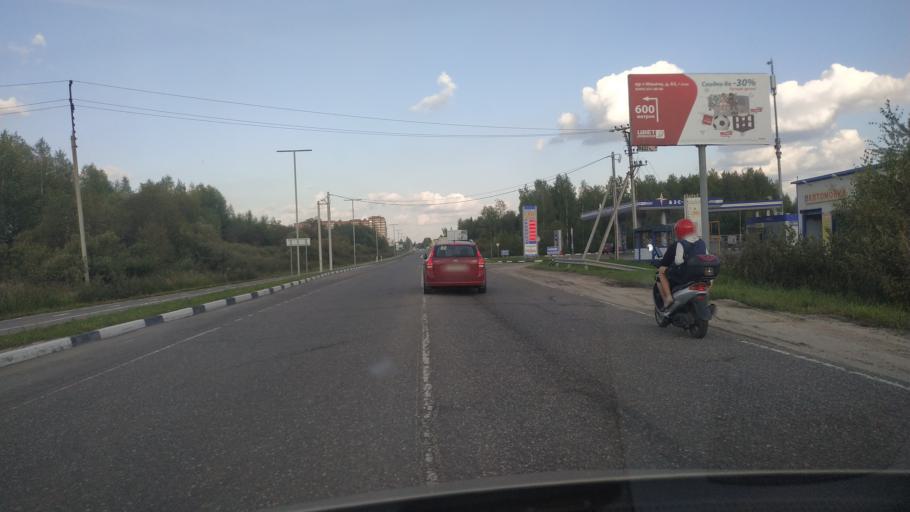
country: RU
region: Moskovskaya
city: Shatura
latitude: 55.5757
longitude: 39.5014
